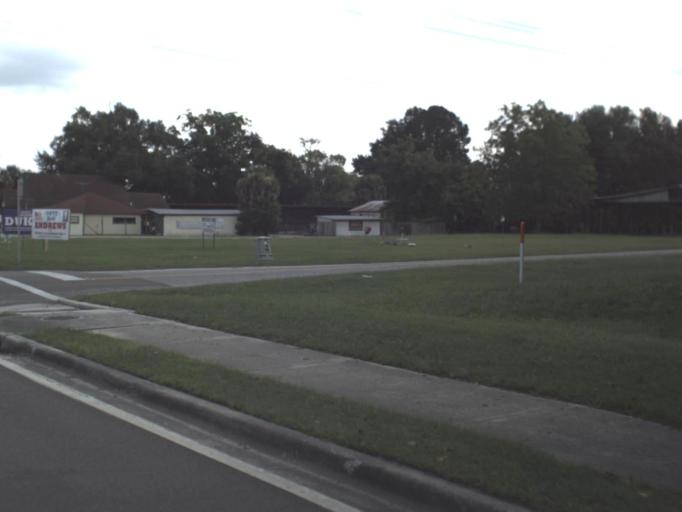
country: US
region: Florida
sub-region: Union County
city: Lake Butler
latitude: 30.0212
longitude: -82.3450
